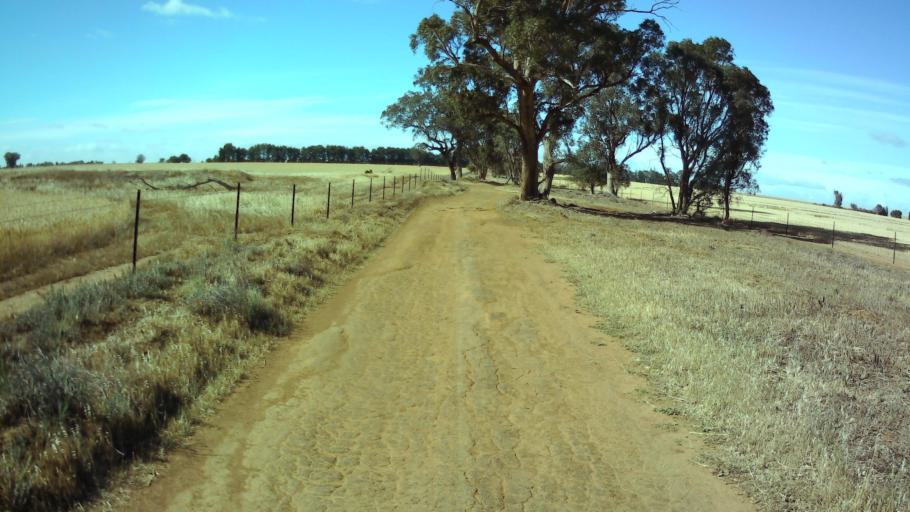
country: AU
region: New South Wales
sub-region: Weddin
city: Grenfell
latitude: -34.0549
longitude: 148.2683
